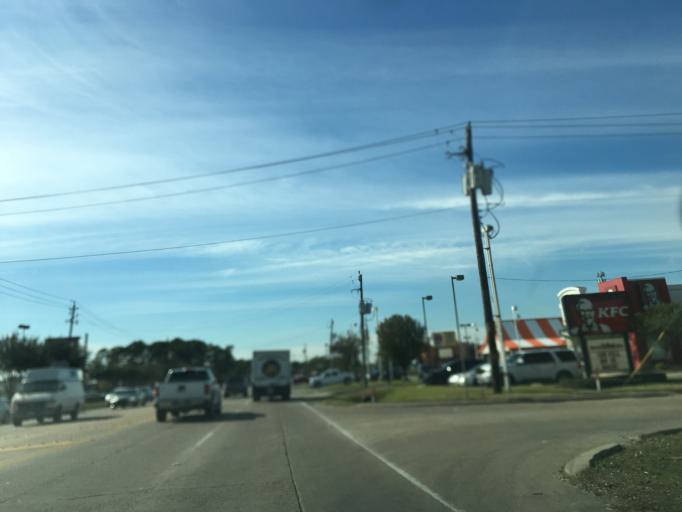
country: US
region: Texas
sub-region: Harris County
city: Cloverleaf
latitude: 29.8079
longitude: -95.1670
